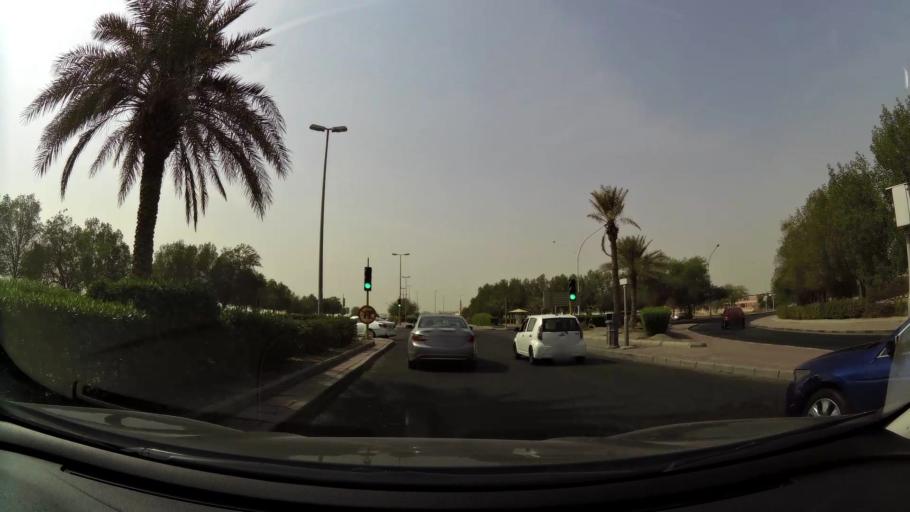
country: KW
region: Al Farwaniyah
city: Al Farwaniyah
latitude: 29.2467
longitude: 47.9348
